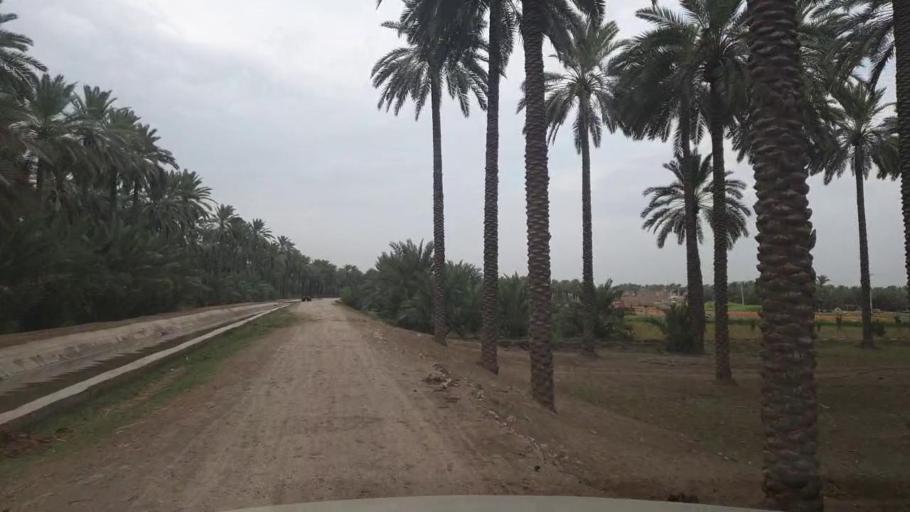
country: PK
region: Sindh
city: Sukkur
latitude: 27.6276
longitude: 68.8203
